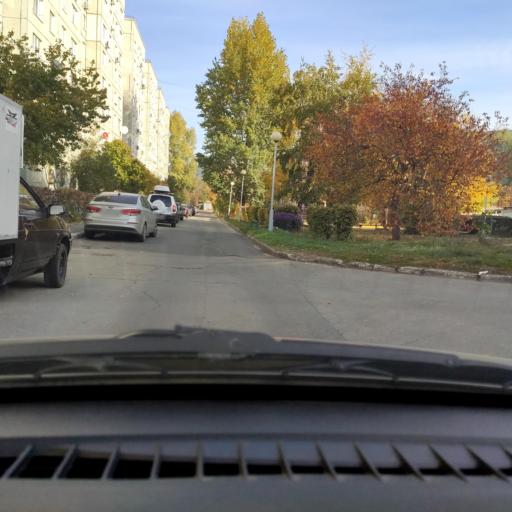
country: RU
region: Samara
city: Tol'yatti
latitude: 53.5423
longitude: 49.3394
